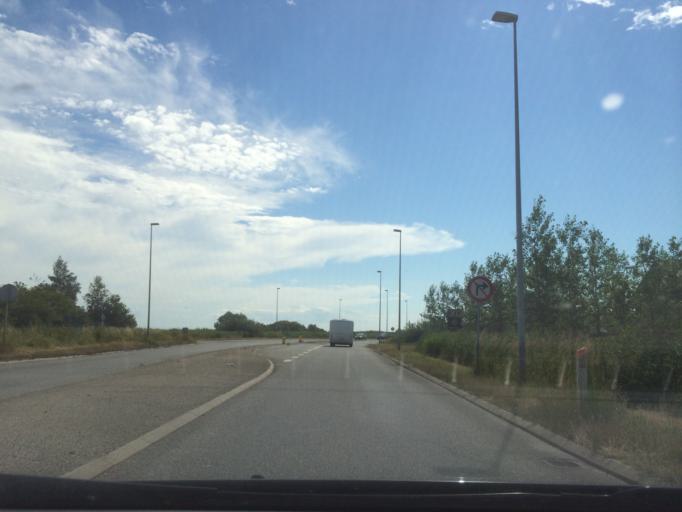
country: DK
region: Zealand
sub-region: Koge Kommune
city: Koge
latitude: 55.4797
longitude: 12.1908
